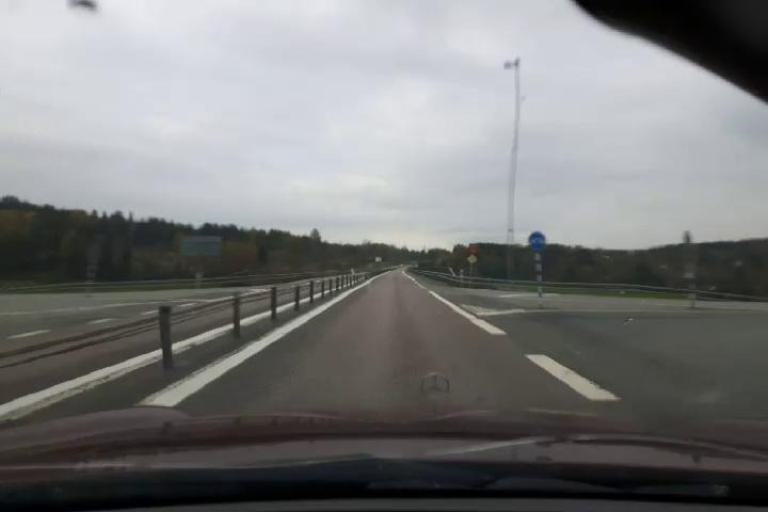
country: SE
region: Vaesternorrland
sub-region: Kramfors Kommun
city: Nordingra
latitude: 62.9223
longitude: 18.0993
